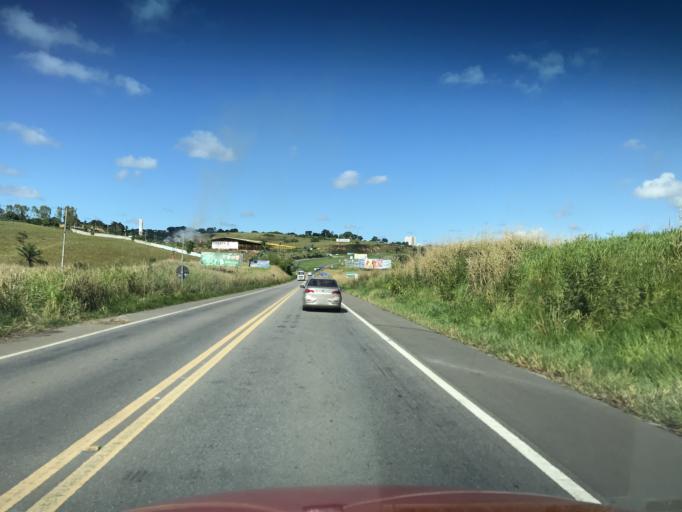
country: BR
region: Bahia
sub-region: Santo Antonio De Jesus
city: Santo Antonio de Jesus
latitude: -12.9451
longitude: -39.2520
